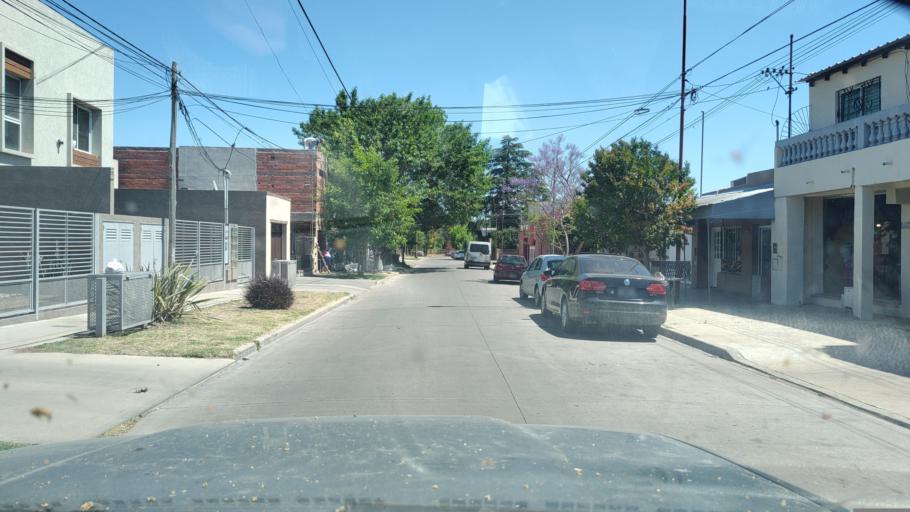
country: AR
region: Buenos Aires
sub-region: Partido de Lujan
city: Lujan
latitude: -34.5827
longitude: -59.1121
